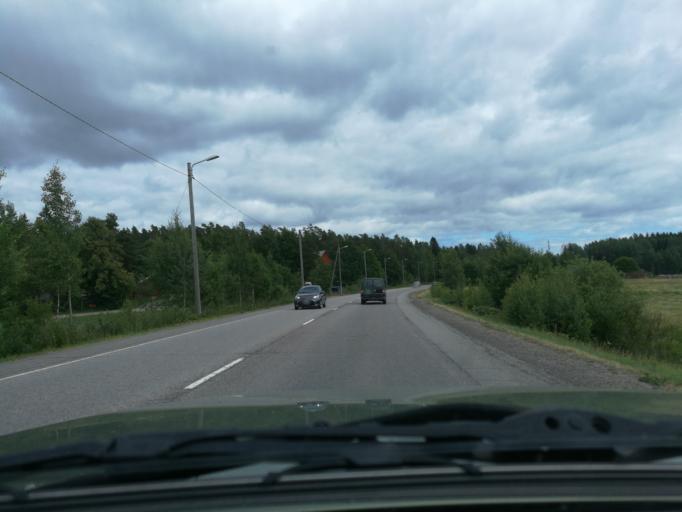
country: FI
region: Uusimaa
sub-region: Helsinki
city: Vantaa
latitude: 60.3135
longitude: 25.0884
